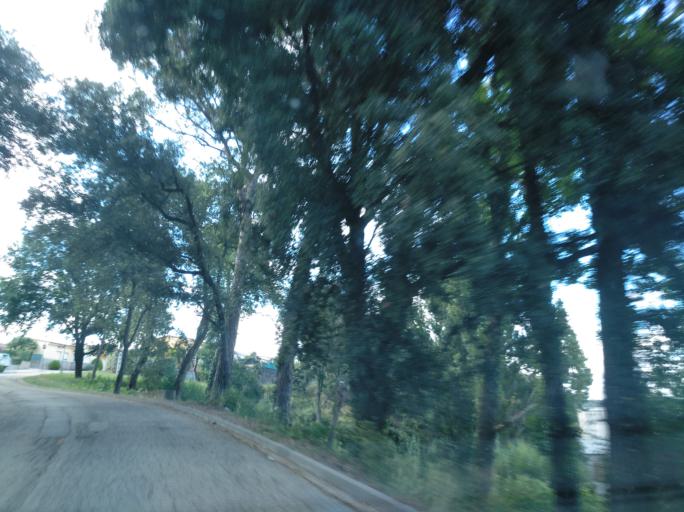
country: ES
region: Catalonia
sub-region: Provincia de Girona
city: Angles
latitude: 41.9705
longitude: 2.6680
